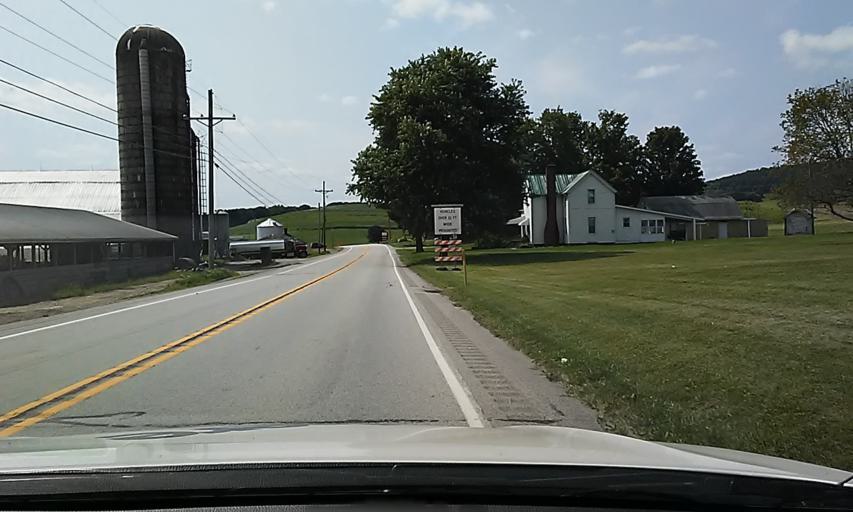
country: US
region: Pennsylvania
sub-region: Indiana County
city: Clymer
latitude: 40.7487
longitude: -79.0875
